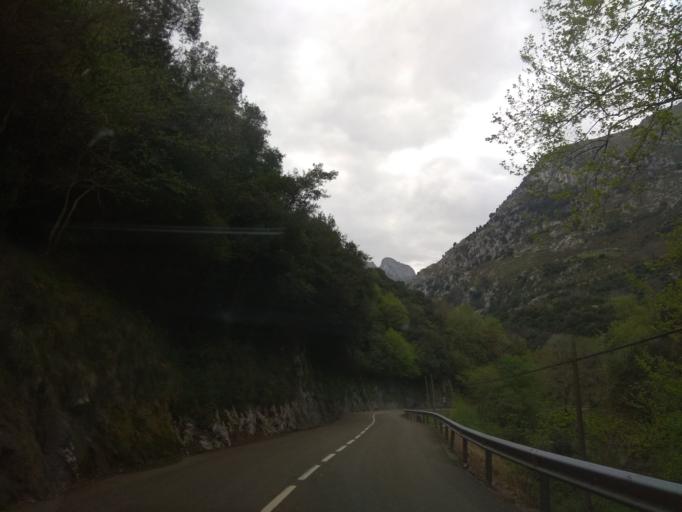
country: ES
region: Cantabria
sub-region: Provincia de Cantabria
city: Tresviso
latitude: 43.3123
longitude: -4.6088
